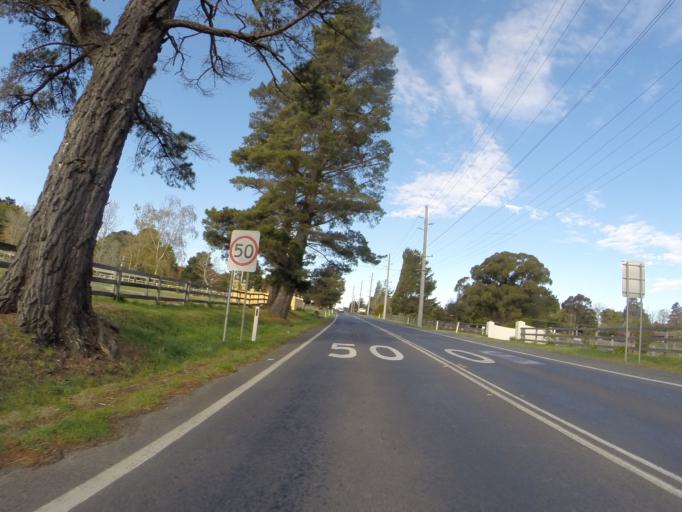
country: AU
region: New South Wales
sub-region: Wingecarribee
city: Moss Vale
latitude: -34.5552
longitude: 150.3546
